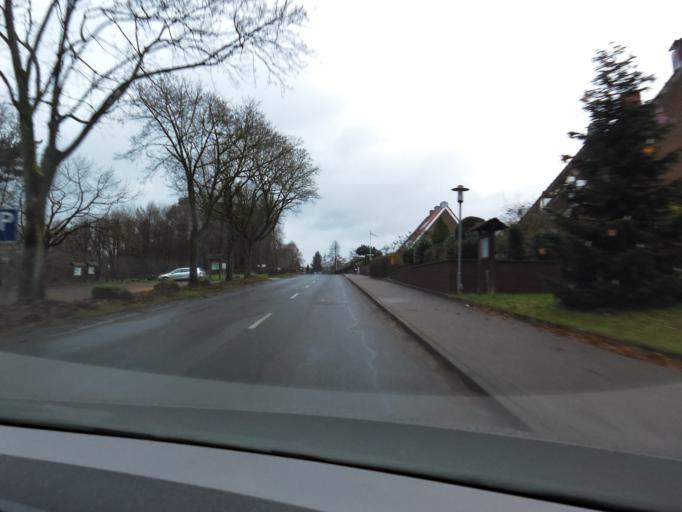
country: DE
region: Schleswig-Holstein
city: Ratzeburg
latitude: 53.7044
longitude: 10.7884
